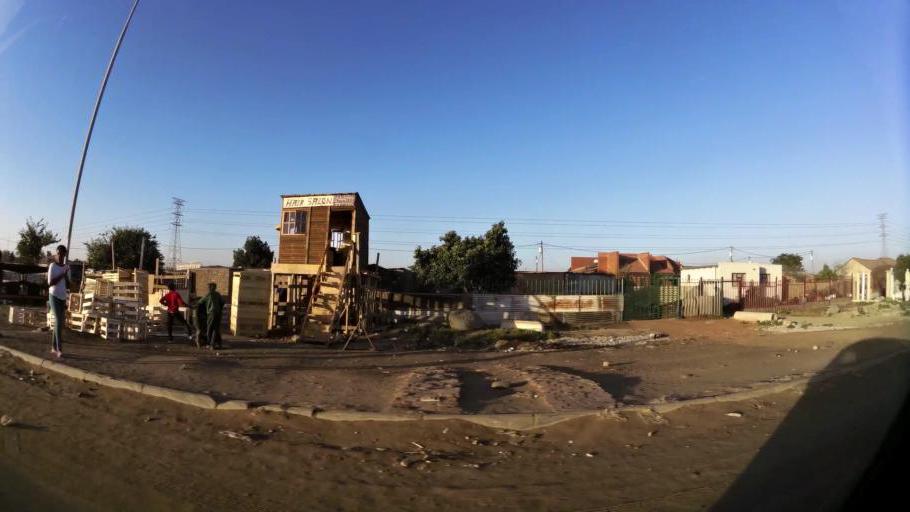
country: ZA
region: North-West
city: Ga-Rankuwa
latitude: -25.5939
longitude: 28.0776
